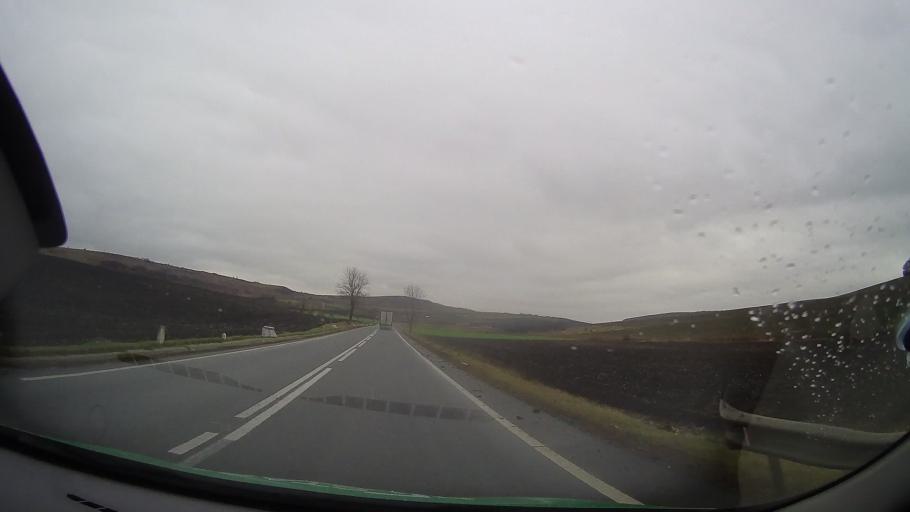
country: RO
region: Mures
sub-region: Comuna Lunca
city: Lunca
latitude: 46.8746
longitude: 24.5453
